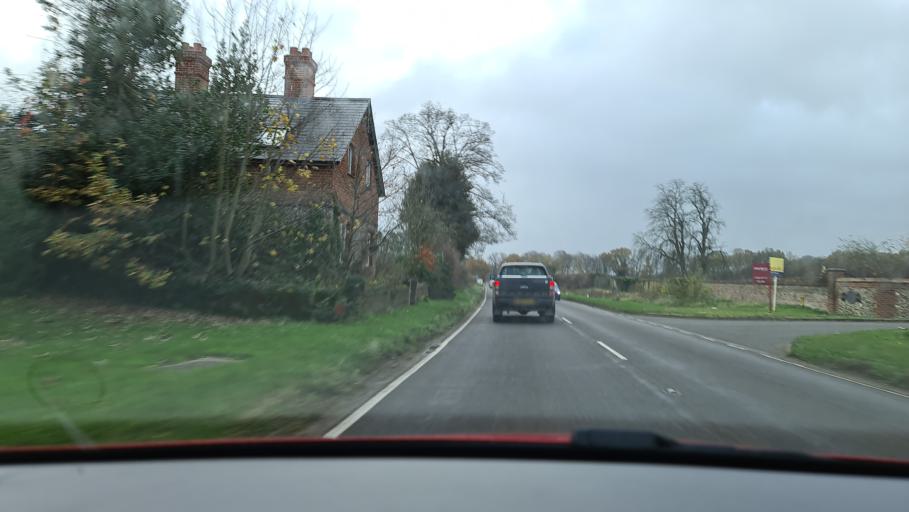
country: GB
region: England
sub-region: Buckinghamshire
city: Great Missenden
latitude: 51.7250
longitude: -0.7241
